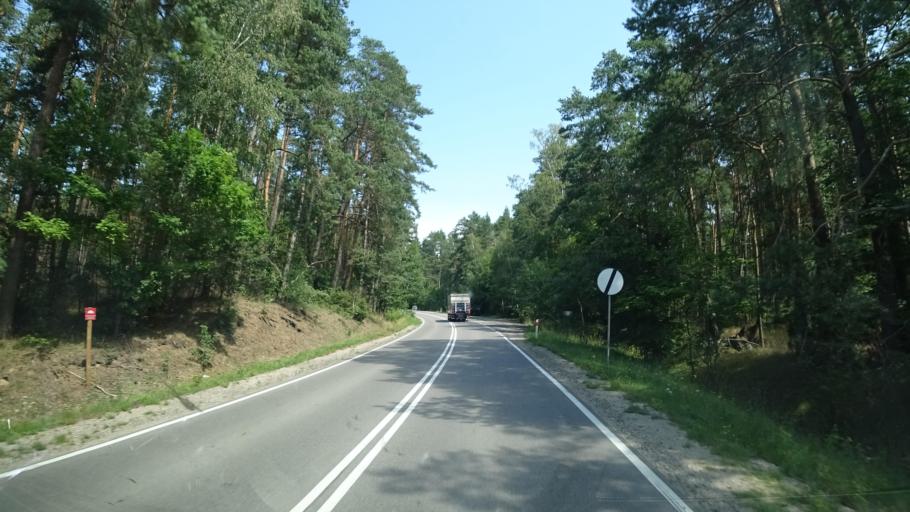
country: PL
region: Pomeranian Voivodeship
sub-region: Powiat koscierski
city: Lipusz
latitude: 54.0891
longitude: 17.8028
